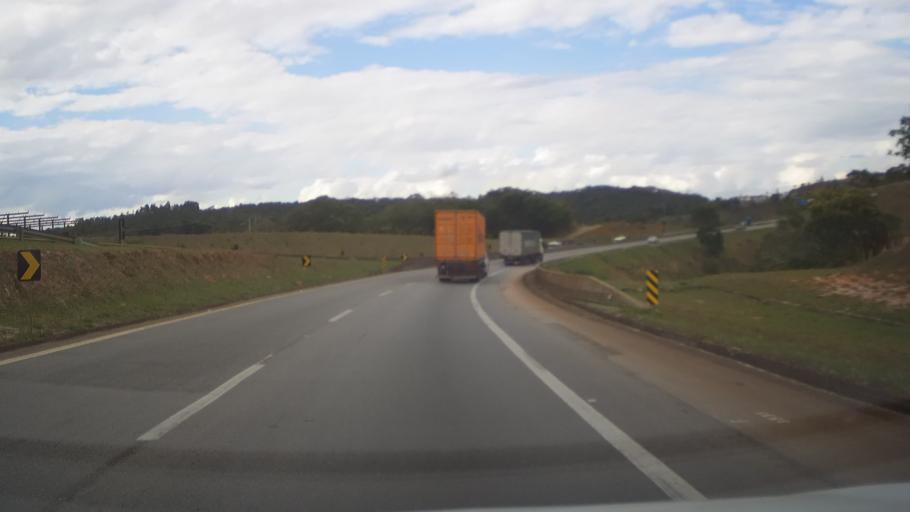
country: BR
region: Minas Gerais
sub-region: Itauna
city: Itauna
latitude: -20.2869
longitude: -44.4353
